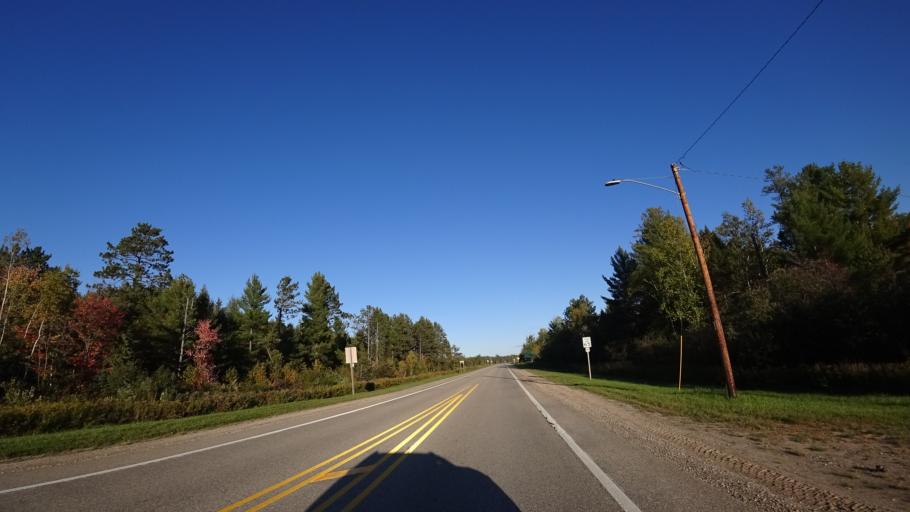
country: US
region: Michigan
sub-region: Luce County
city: Newberry
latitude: 46.3457
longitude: -85.9429
